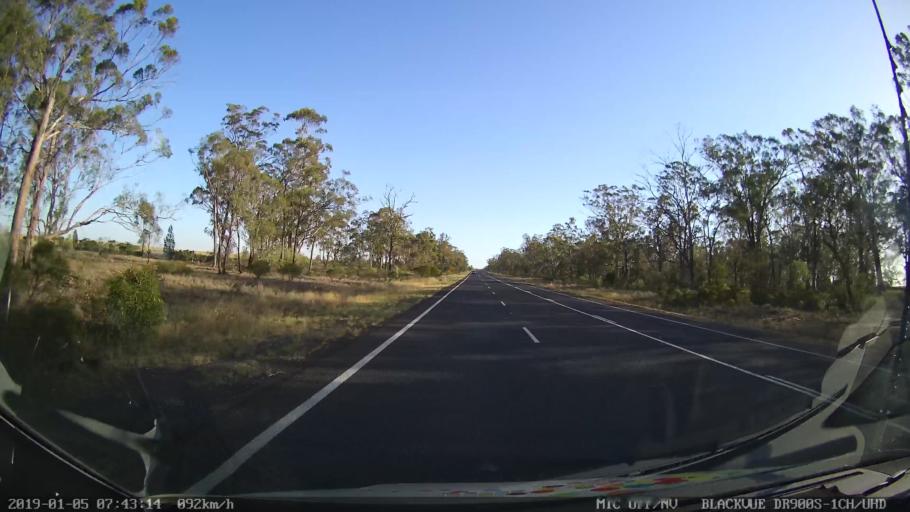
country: AU
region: New South Wales
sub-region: Gilgandra
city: Gilgandra
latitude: -31.8876
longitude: 148.6325
